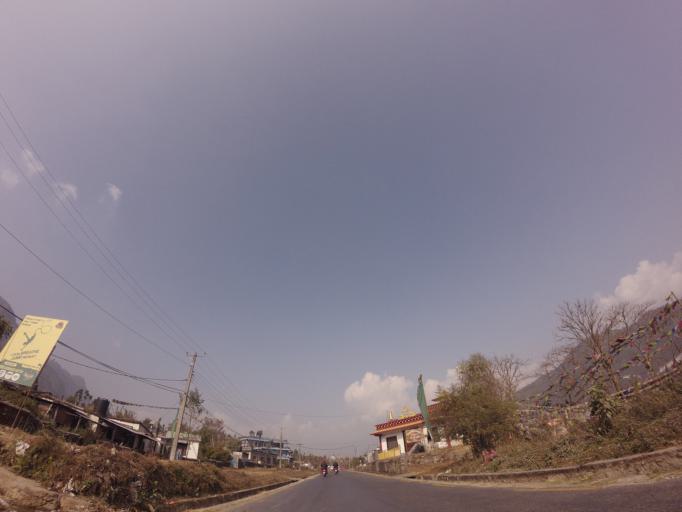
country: NP
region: Western Region
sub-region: Gandaki Zone
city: Pokhara
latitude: 28.2633
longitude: 83.9570
